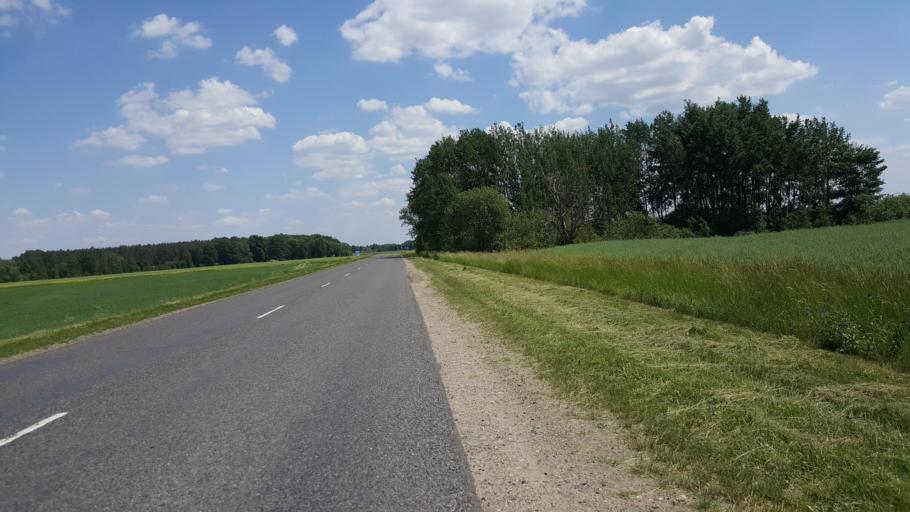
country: BY
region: Brest
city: Kobryn
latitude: 52.2244
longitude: 24.2821
